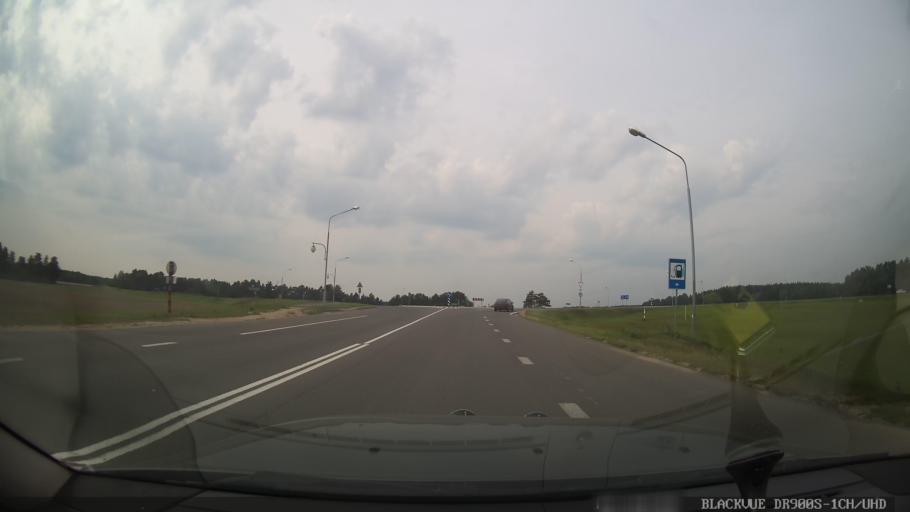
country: BY
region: Grodnenskaya
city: Astravyets
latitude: 54.6115
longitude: 26.0160
